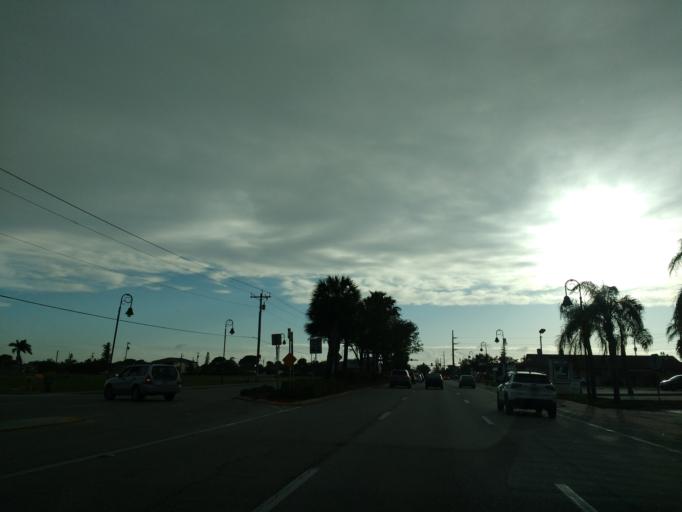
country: US
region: Florida
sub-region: Lee County
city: Cape Coral
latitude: 26.5628
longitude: -81.9639
